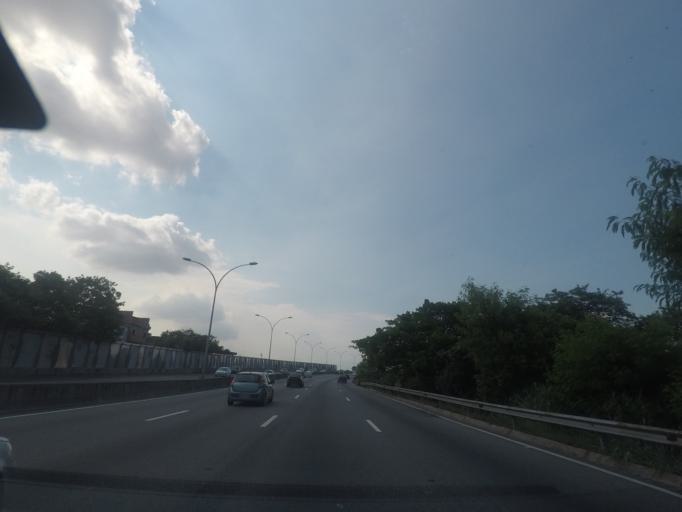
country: BR
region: Rio de Janeiro
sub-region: Rio De Janeiro
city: Rio de Janeiro
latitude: -22.8502
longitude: -43.2405
